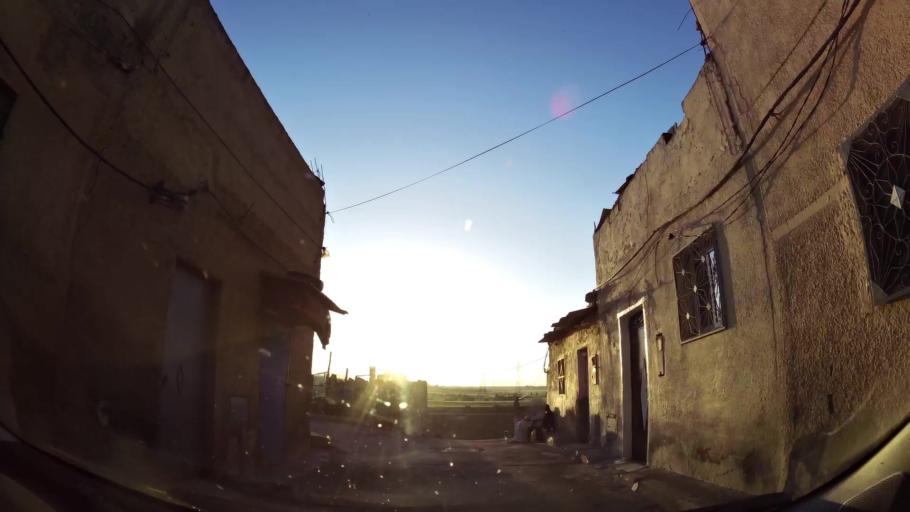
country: MA
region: Oriental
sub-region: Oujda-Angad
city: Oujda
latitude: 34.7049
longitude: -1.9233
